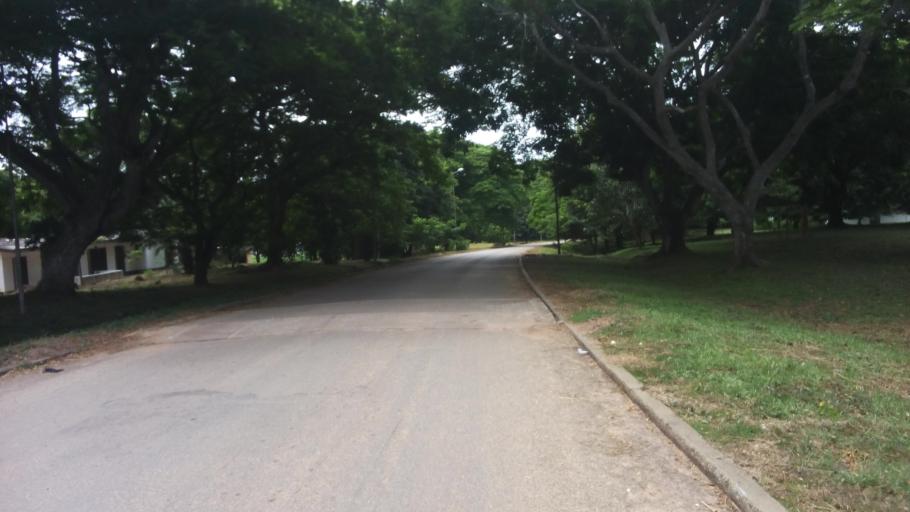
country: GH
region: Central
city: Cape Coast
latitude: 5.1269
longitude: -1.2910
